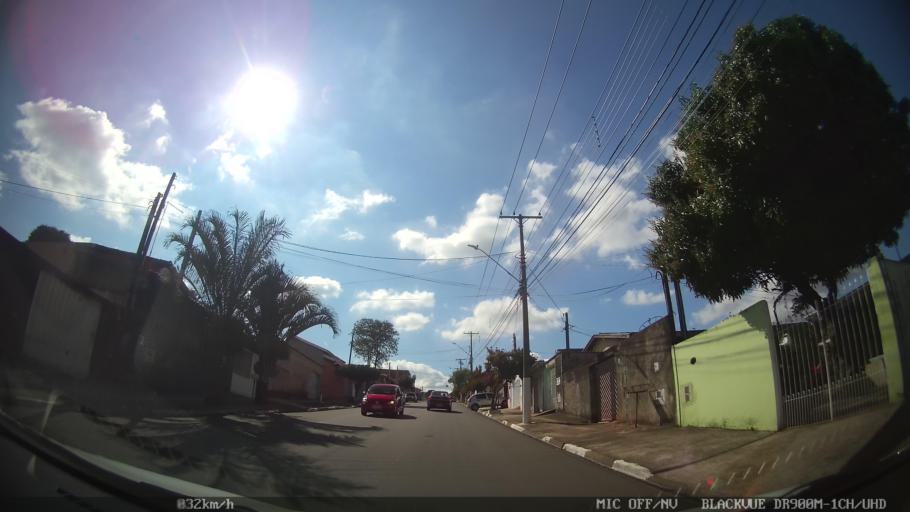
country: BR
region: Sao Paulo
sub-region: Hortolandia
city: Hortolandia
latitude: -22.8902
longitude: -47.1947
